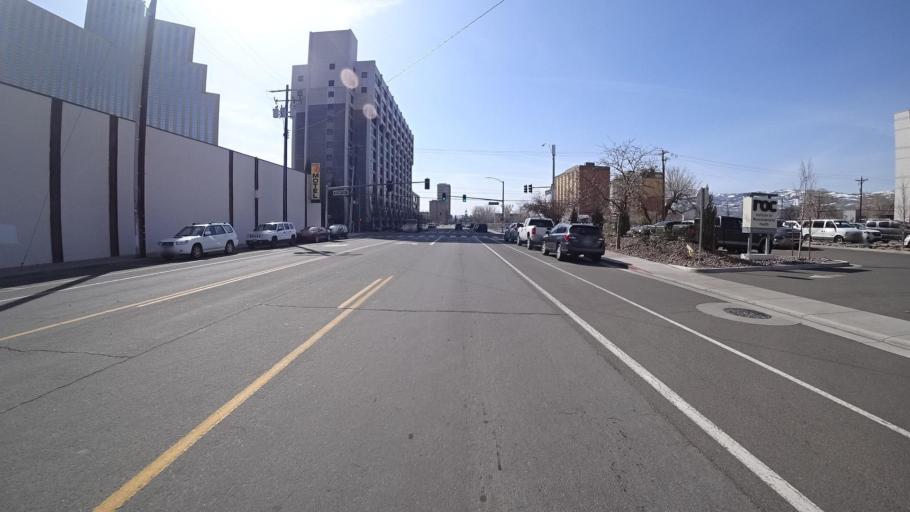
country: US
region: Nevada
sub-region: Washoe County
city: Reno
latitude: 39.5308
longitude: -119.8188
